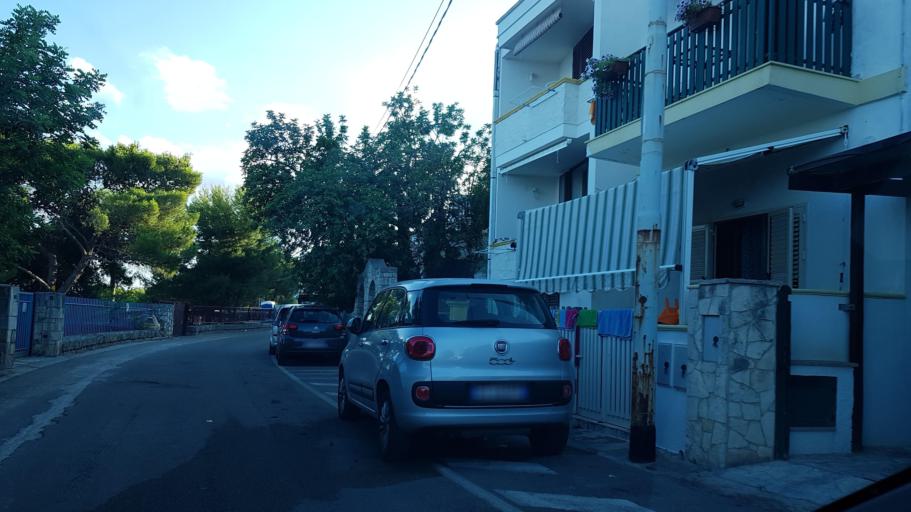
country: IT
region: Apulia
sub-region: Provincia di Lecce
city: Castro
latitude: 39.9970
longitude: 18.4183
